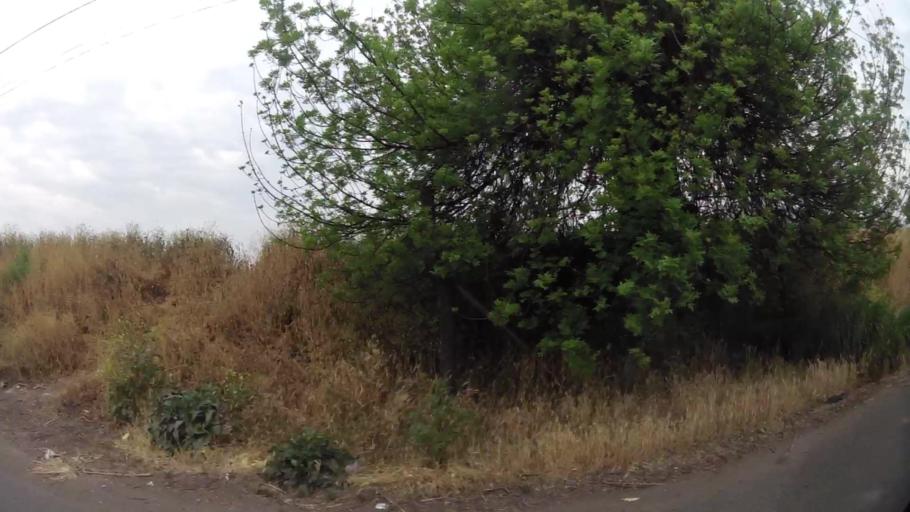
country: CL
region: Santiago Metropolitan
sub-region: Provincia de Chacabuco
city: Chicureo Abajo
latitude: -33.2604
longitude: -70.7619
